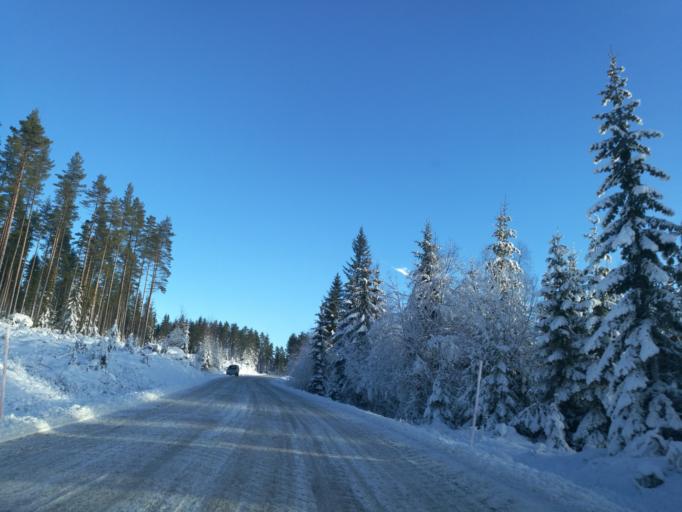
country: NO
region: Hedmark
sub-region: Grue
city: Kirkenaer
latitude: 60.4549
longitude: 12.5081
